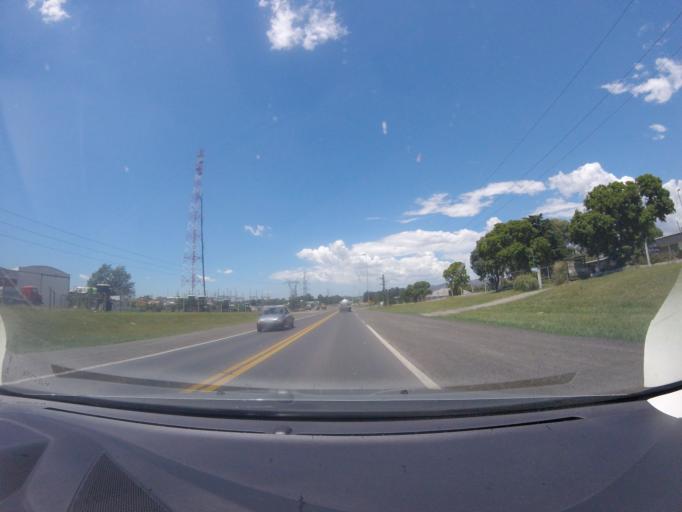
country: AR
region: Buenos Aires
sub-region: Partido de Tandil
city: Tandil
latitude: -37.2953
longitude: -59.1366
